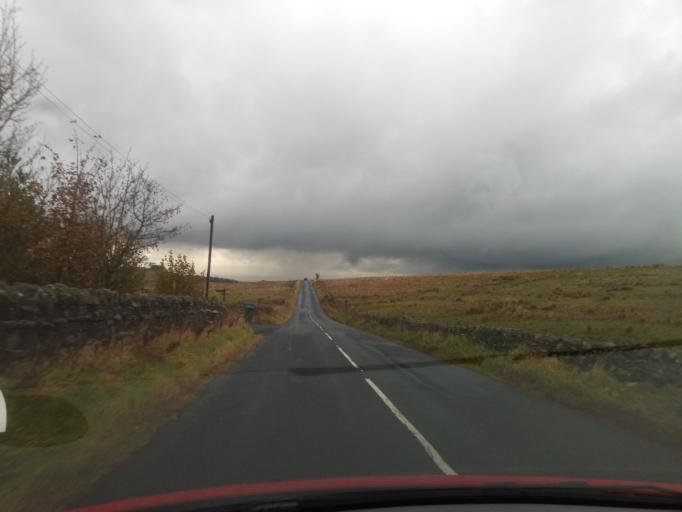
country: GB
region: England
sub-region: Northumberland
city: Corsenside
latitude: 55.1752
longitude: -2.2593
